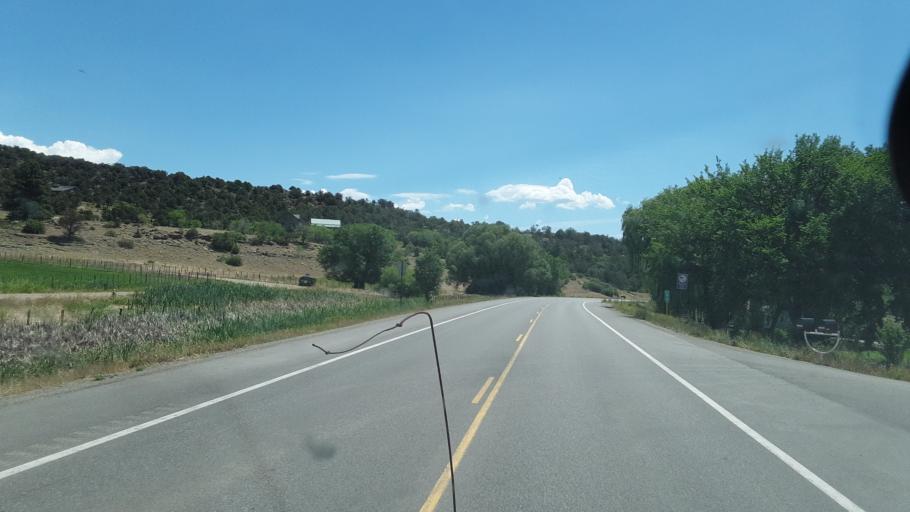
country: US
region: Colorado
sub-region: La Plata County
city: Bayfield
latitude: 37.2258
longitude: -107.6621
